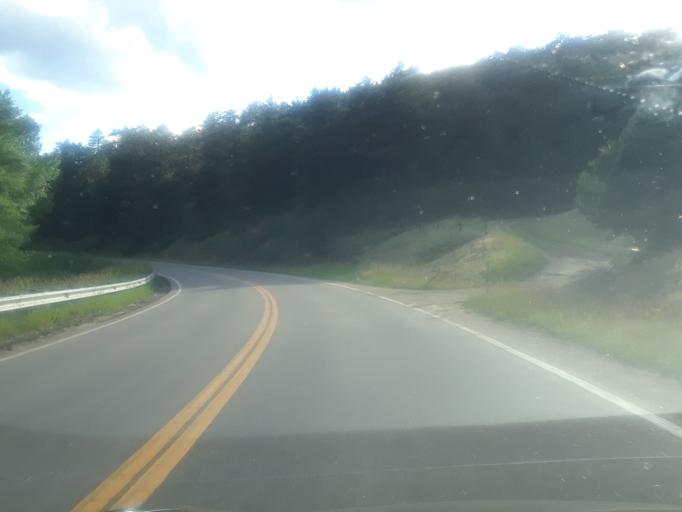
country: US
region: Colorado
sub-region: Jefferson County
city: Kittredge
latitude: 39.7186
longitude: -105.3738
